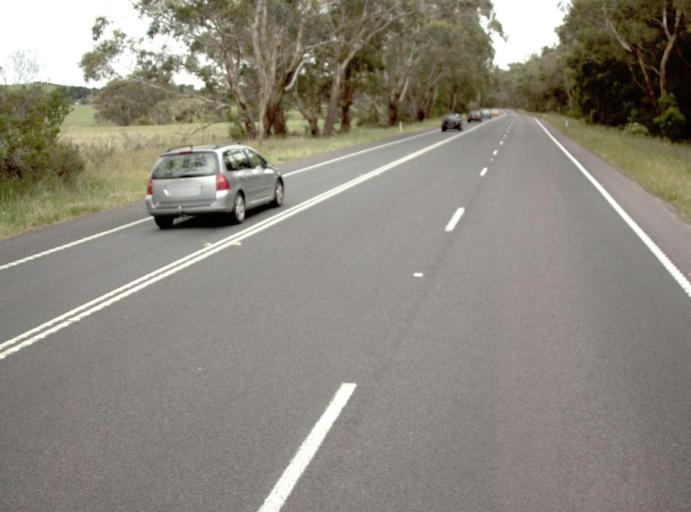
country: AU
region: Victoria
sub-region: Bass Coast
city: North Wonthaggi
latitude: -38.5725
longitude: 145.9769
